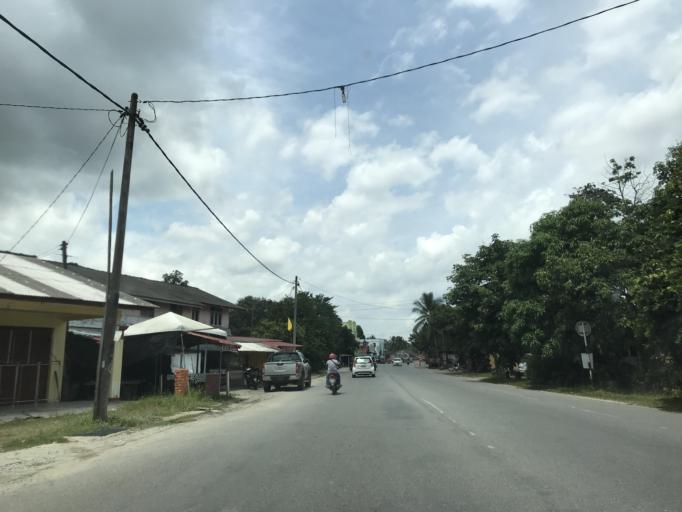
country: MY
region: Kelantan
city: Kota Bharu
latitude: 6.0784
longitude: 102.2084
